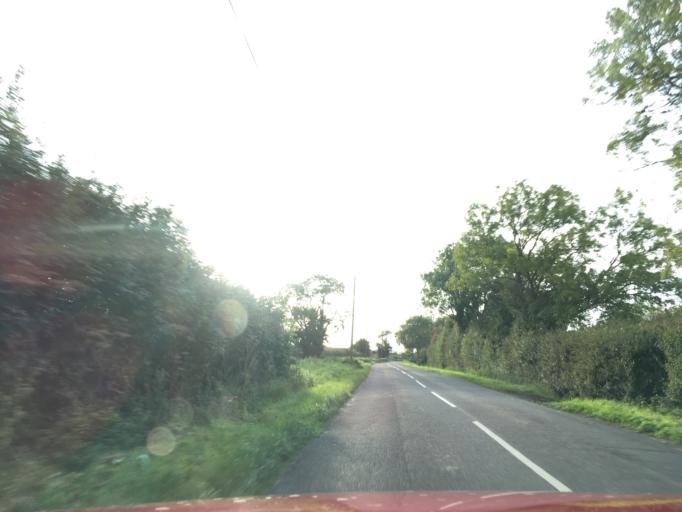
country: GB
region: England
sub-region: South Gloucestershire
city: Almondsbury
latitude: 51.5683
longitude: -2.6097
